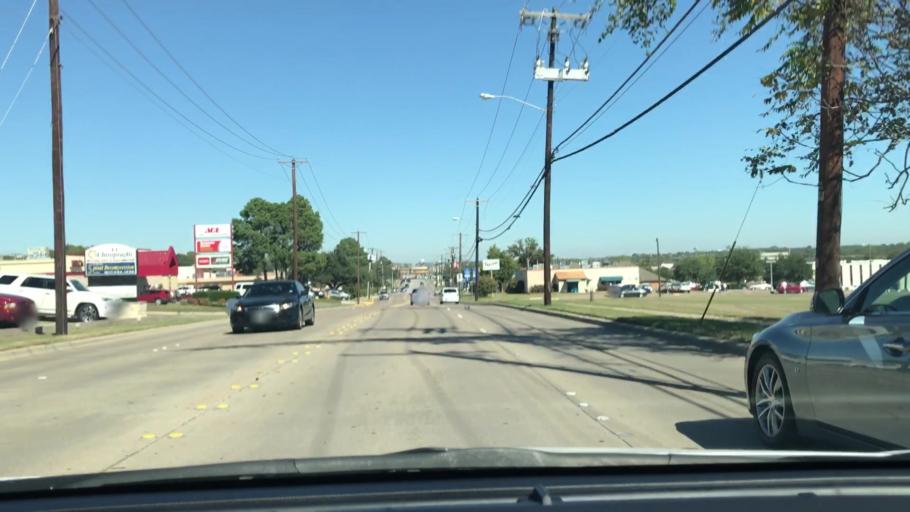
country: US
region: Texas
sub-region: Tarrant County
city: Hurst
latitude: 32.8315
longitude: -97.1863
